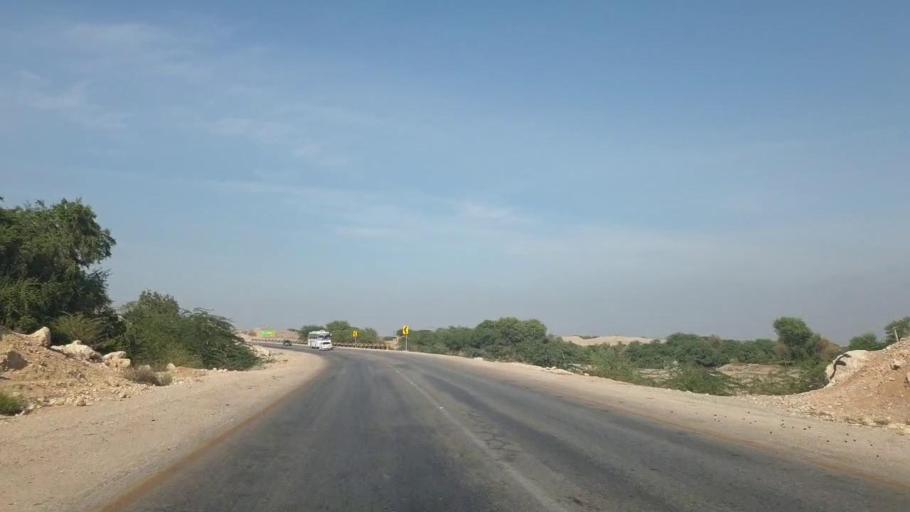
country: PK
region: Sindh
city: Sehwan
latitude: 26.2984
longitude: 67.8948
